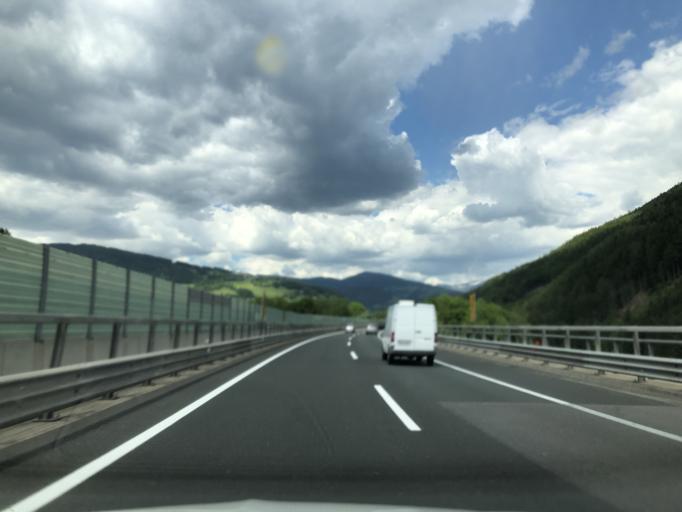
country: AT
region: Carinthia
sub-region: Politischer Bezirk Spittal an der Drau
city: Trebesing
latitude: 46.8744
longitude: 13.5066
